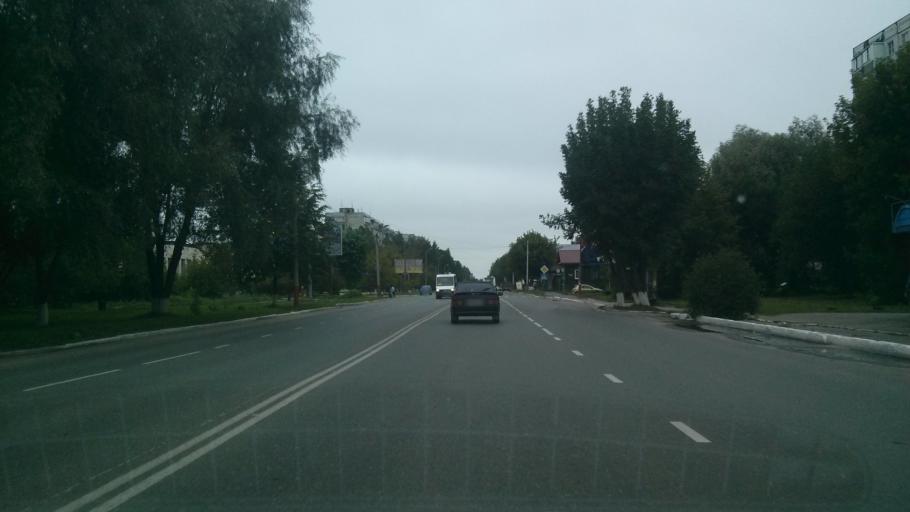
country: RU
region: Vladimir
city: Murom
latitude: 55.5683
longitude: 42.0604
